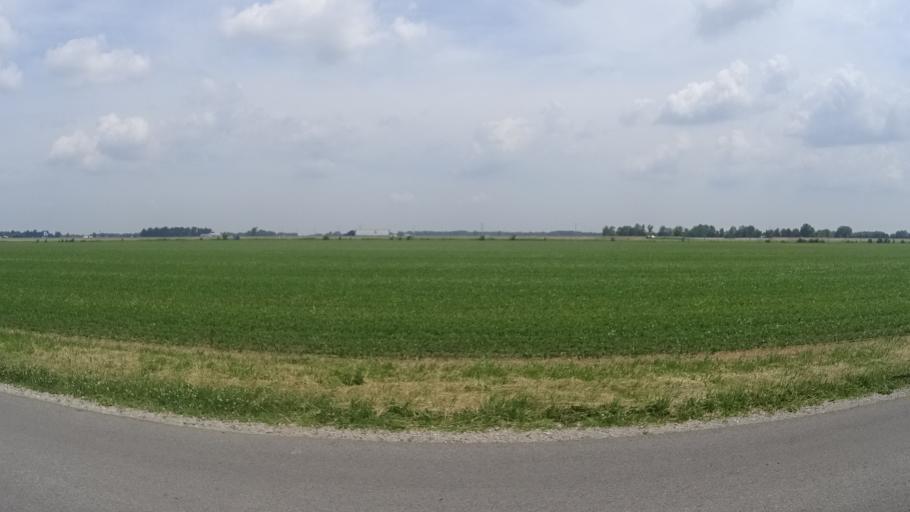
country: US
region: Ohio
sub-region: Huron County
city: Monroeville
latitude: 41.3336
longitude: -82.7112
